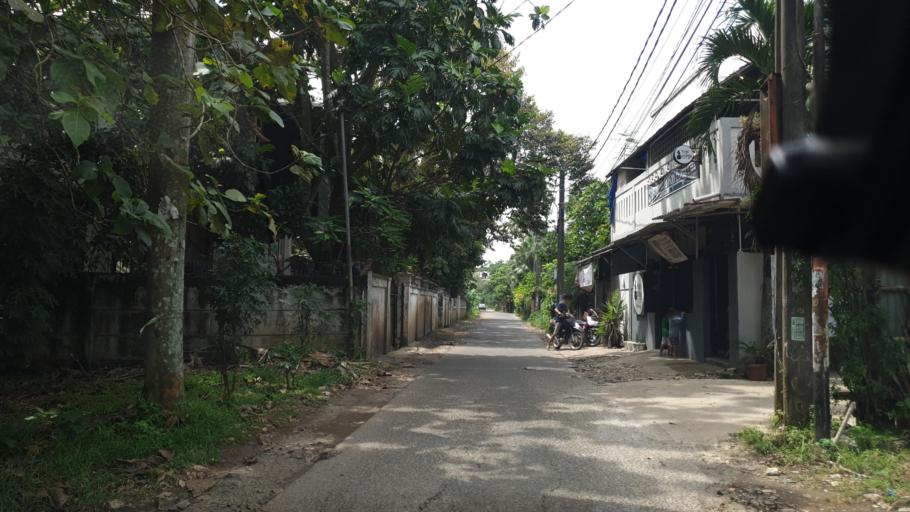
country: ID
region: West Java
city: Pamulang
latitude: -6.3636
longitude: 106.7644
